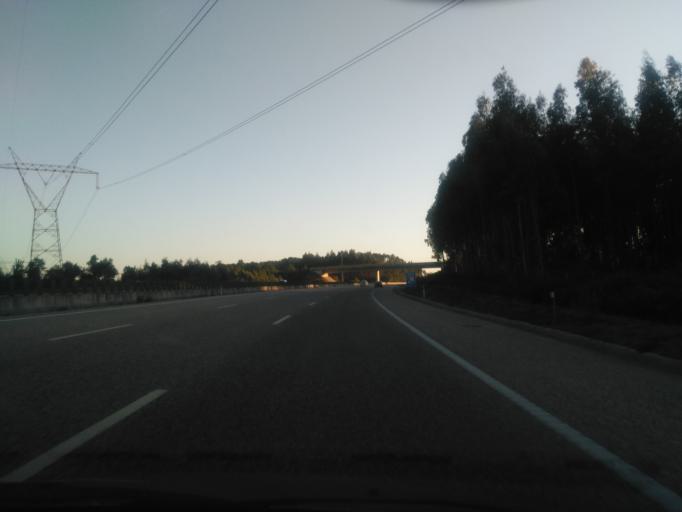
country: PT
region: Leiria
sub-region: Leiria
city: Monte Redondo
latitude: 39.9369
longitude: -8.7716
